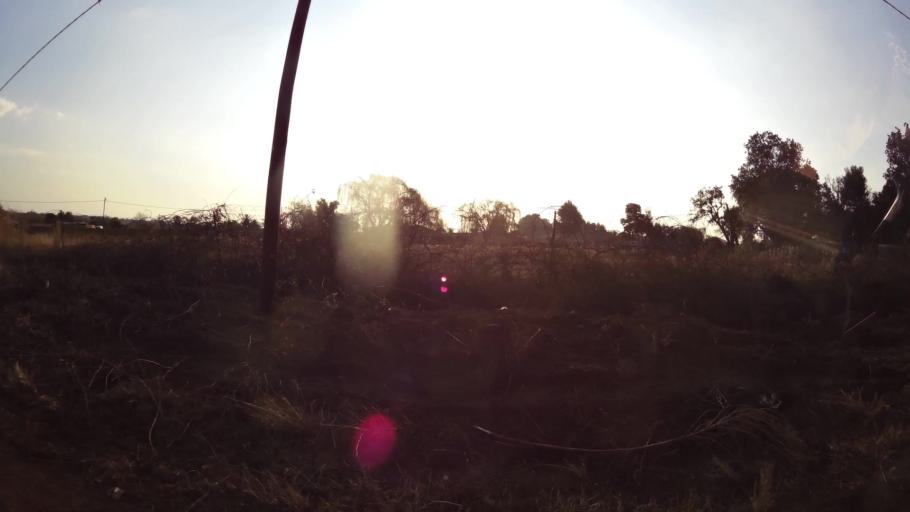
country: ZA
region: Gauteng
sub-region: Ekurhuleni Metropolitan Municipality
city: Benoni
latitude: -26.1571
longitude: 28.3687
